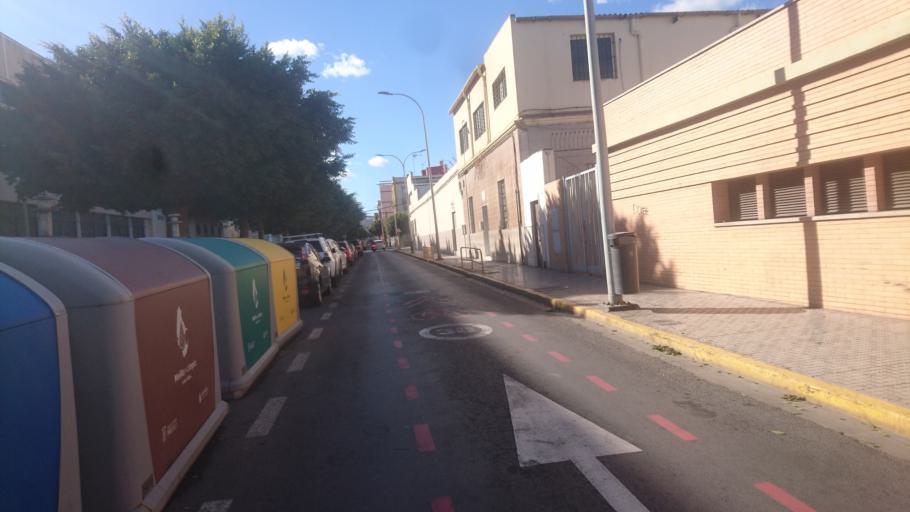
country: ES
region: Melilla
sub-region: Melilla
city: Melilla
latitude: 35.2781
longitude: -2.9391
